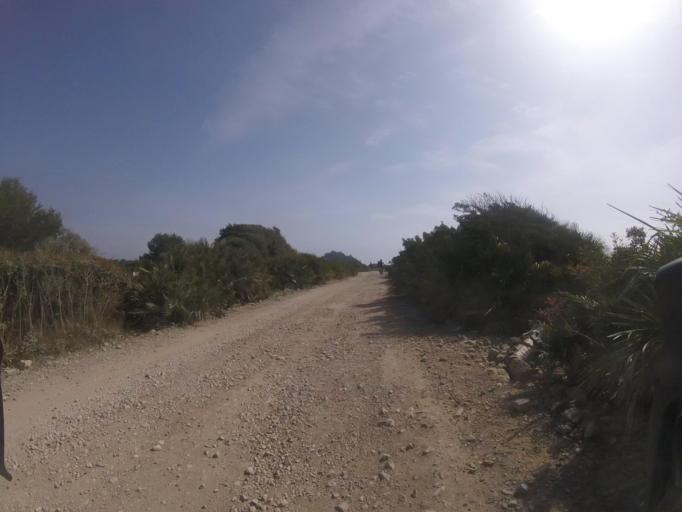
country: ES
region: Valencia
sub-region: Provincia de Castello
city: Santa Magdalena de Pulpis
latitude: 40.2955
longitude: 0.3436
